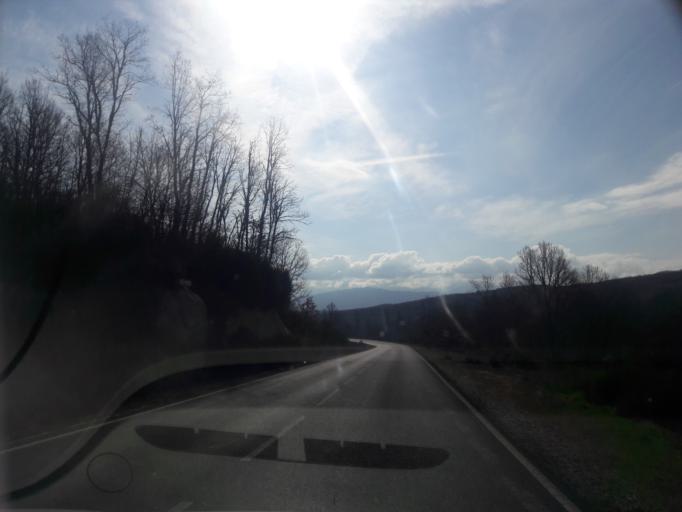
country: ES
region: Castille and Leon
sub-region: Provincia de Salamanca
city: Horcajo de Montemayor
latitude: 40.4137
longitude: -5.9239
